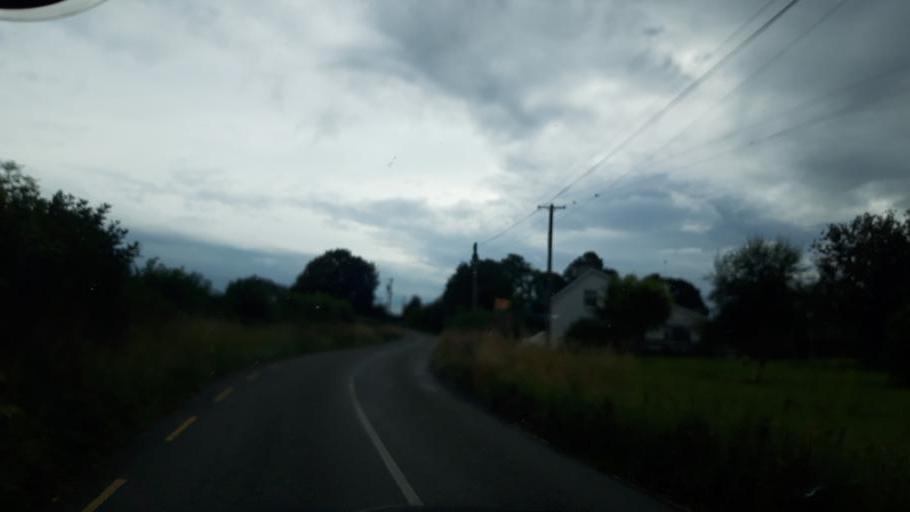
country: IE
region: Leinster
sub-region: Kilkenny
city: Ballyragget
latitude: 52.7767
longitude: -7.3469
